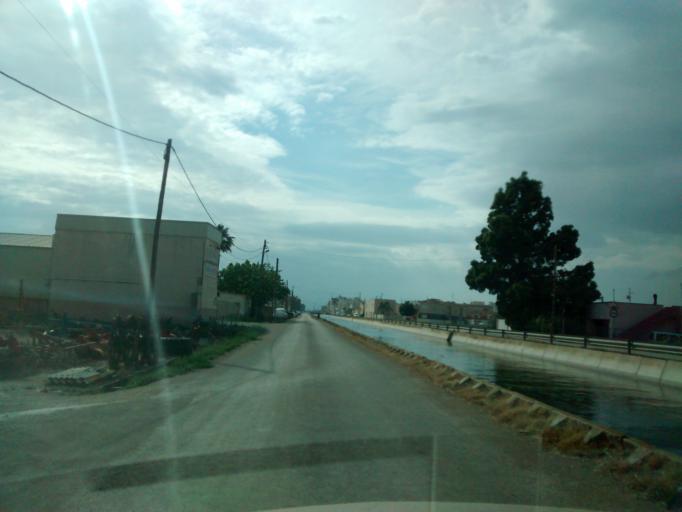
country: ES
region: Catalonia
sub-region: Provincia de Tarragona
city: Deltebre
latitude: 40.7026
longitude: 0.7242
